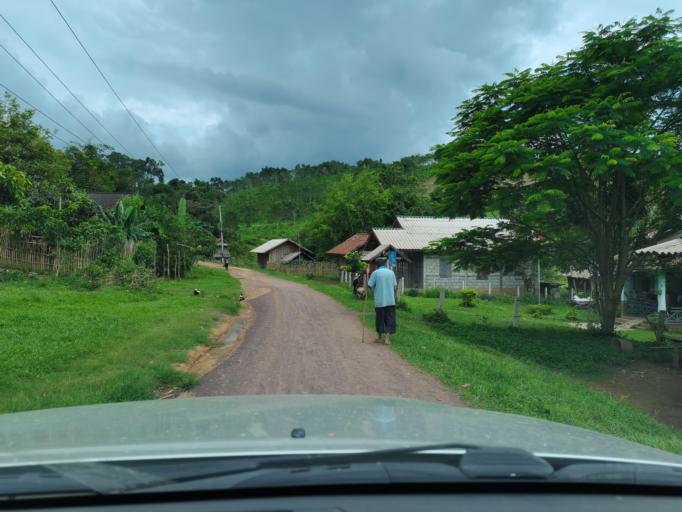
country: LA
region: Loungnamtha
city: Muang Long
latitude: 20.7052
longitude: 101.0103
